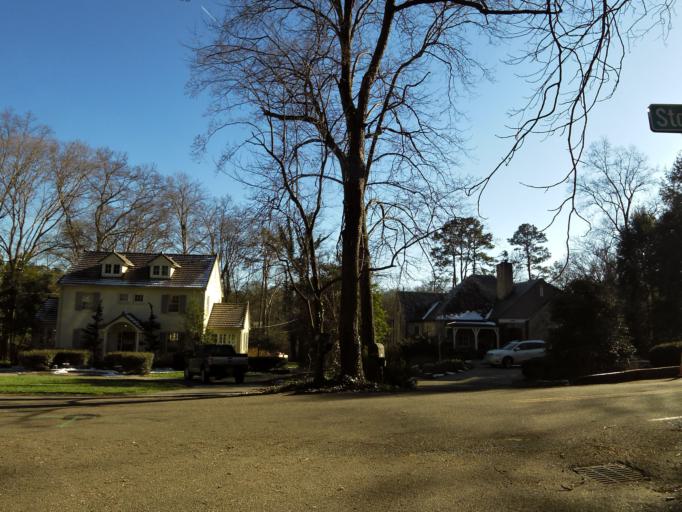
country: US
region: Tennessee
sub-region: Knox County
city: Knoxville
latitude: 35.9186
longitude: -84.0132
